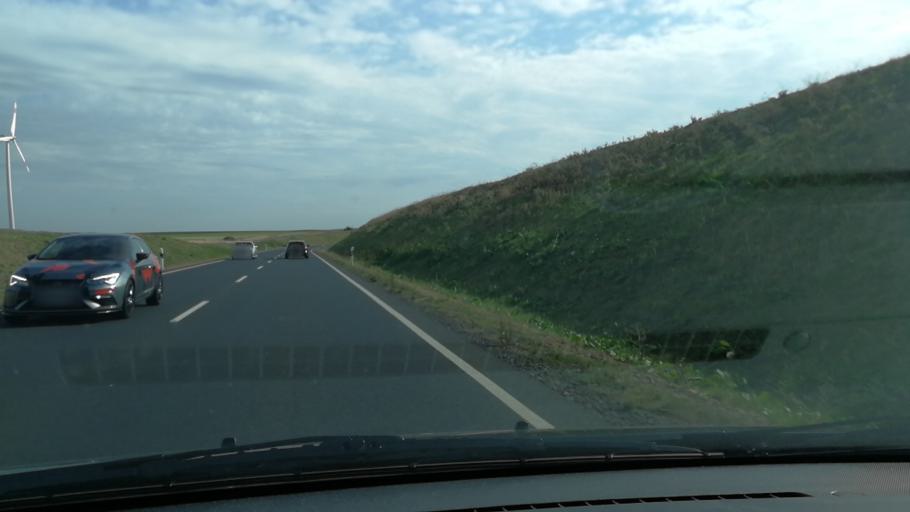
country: DE
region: Hesse
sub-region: Regierungsbezirk Darmstadt
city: Friedberg
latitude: 50.3025
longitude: 8.7606
